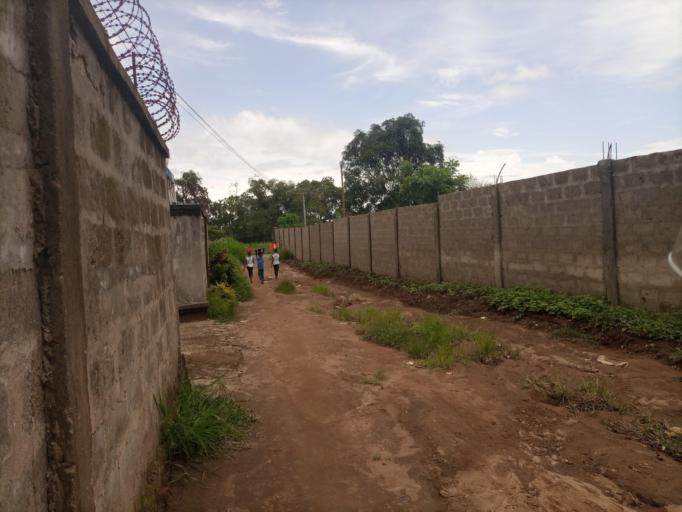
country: SL
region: Northern Province
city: Masoyila
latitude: 8.5924
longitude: -13.1668
